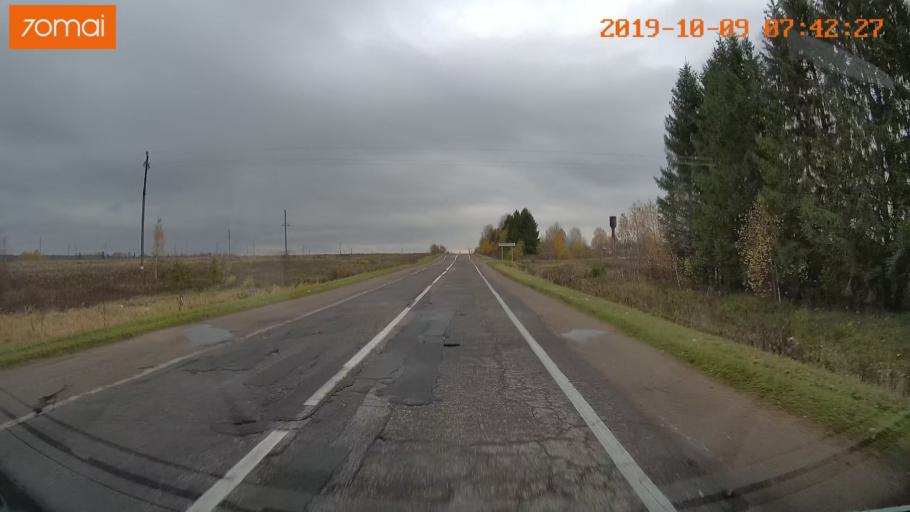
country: RU
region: Jaroslavl
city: Kukoboy
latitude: 58.6429
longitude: 39.7220
